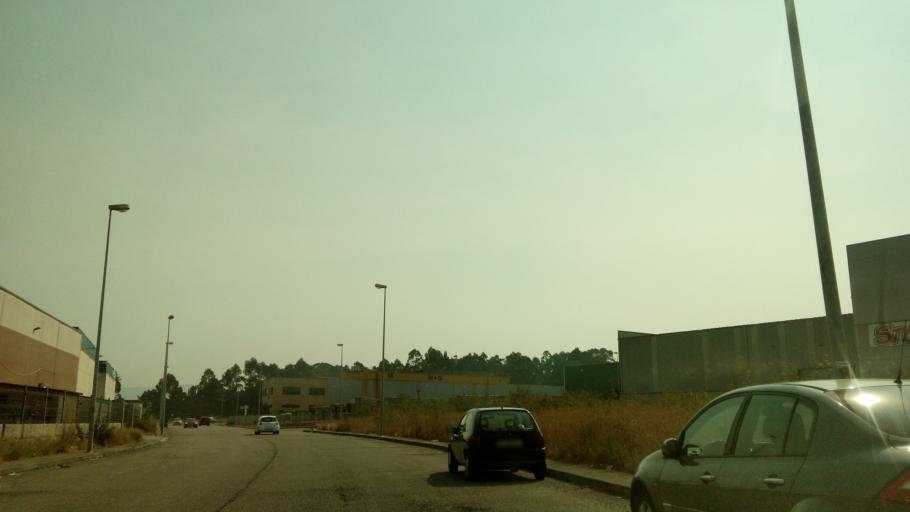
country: PT
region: Viana do Castelo
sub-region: Valenca
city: Valenca
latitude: 42.0397
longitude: -8.6628
